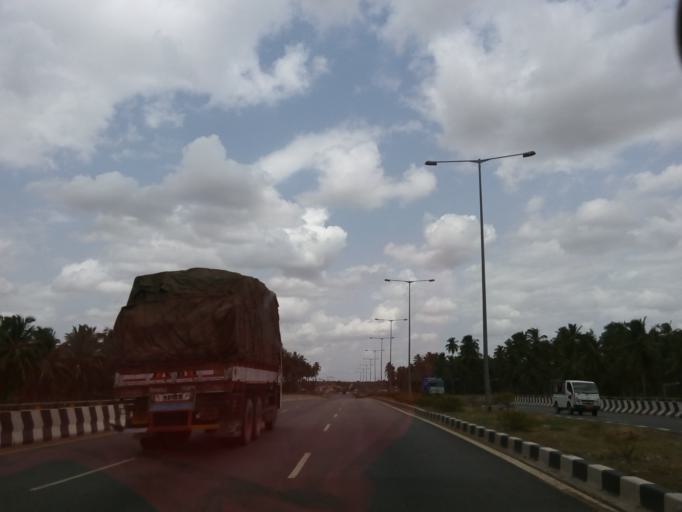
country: IN
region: Karnataka
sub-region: Chitradurga
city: Hiriyur
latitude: 13.9163
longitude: 76.6560
